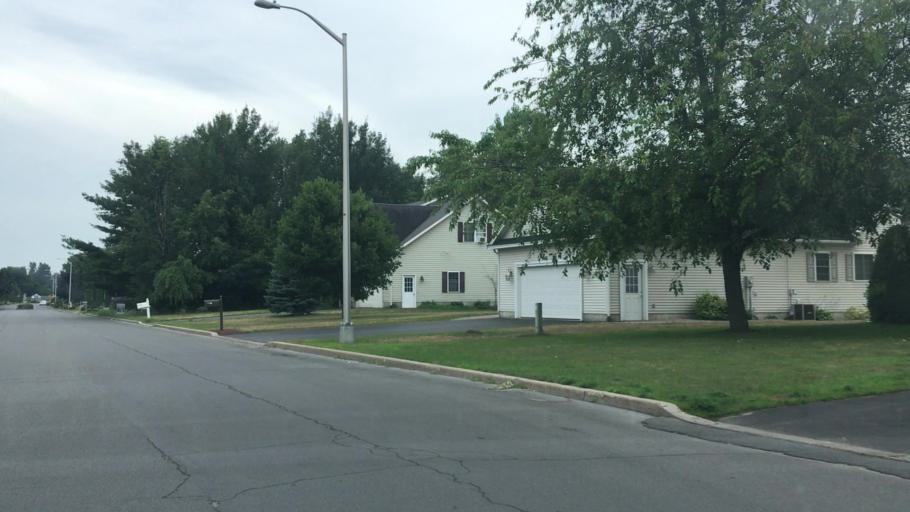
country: US
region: New York
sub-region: Clinton County
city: Plattsburgh West
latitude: 44.6920
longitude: -73.4828
